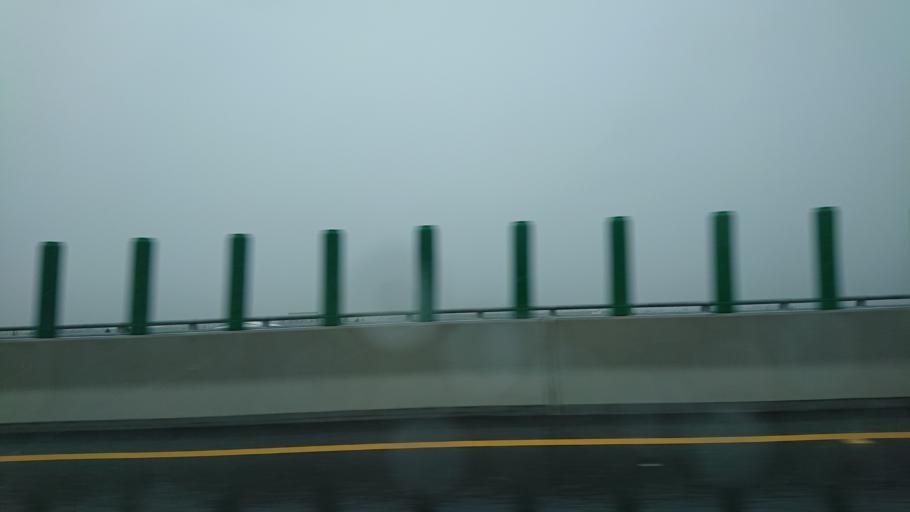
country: TW
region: Taiwan
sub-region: Changhua
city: Chang-hua
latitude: 23.9156
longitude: 120.3100
